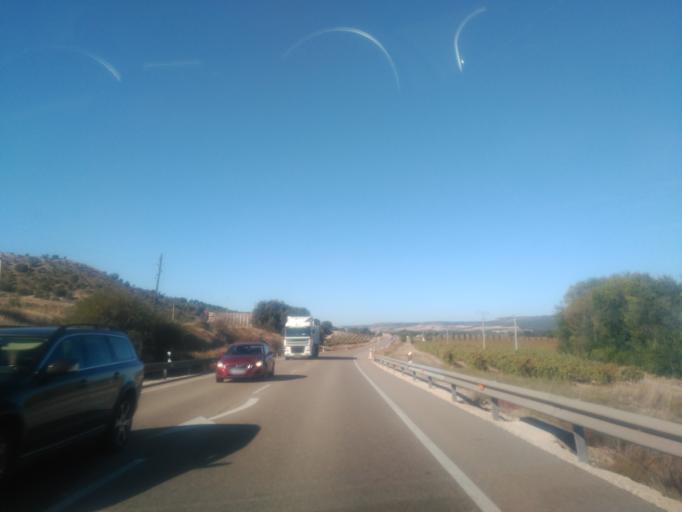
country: ES
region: Castille and Leon
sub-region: Provincia de Valladolid
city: Valbuena de Duero
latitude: 41.6251
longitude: -4.2750
